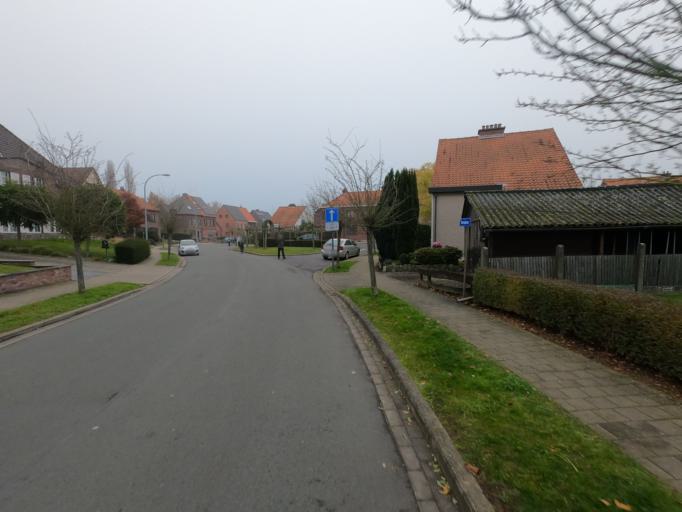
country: BE
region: Flanders
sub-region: Provincie Oost-Vlaanderen
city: Temse
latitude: 51.1323
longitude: 4.2278
